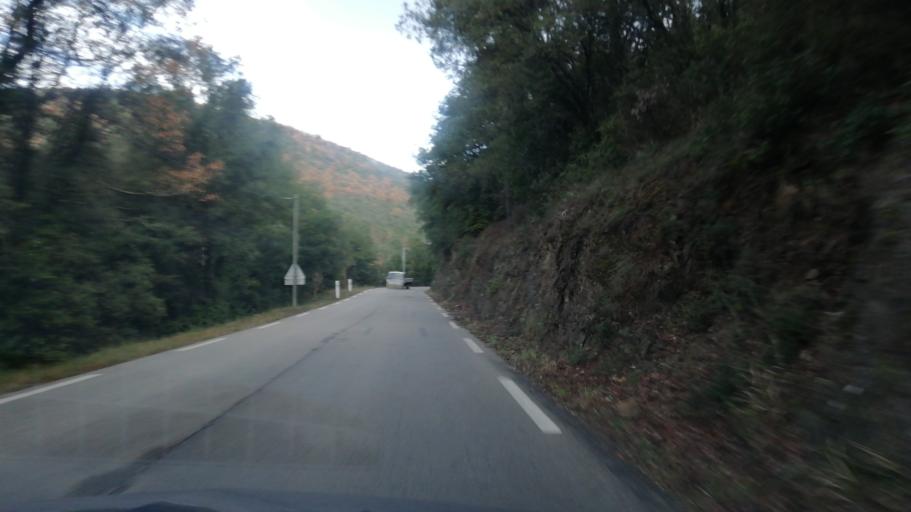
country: FR
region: Languedoc-Roussillon
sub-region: Departement du Gard
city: Saint-Hippolyte-du-Fort
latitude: 43.9786
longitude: 3.8502
